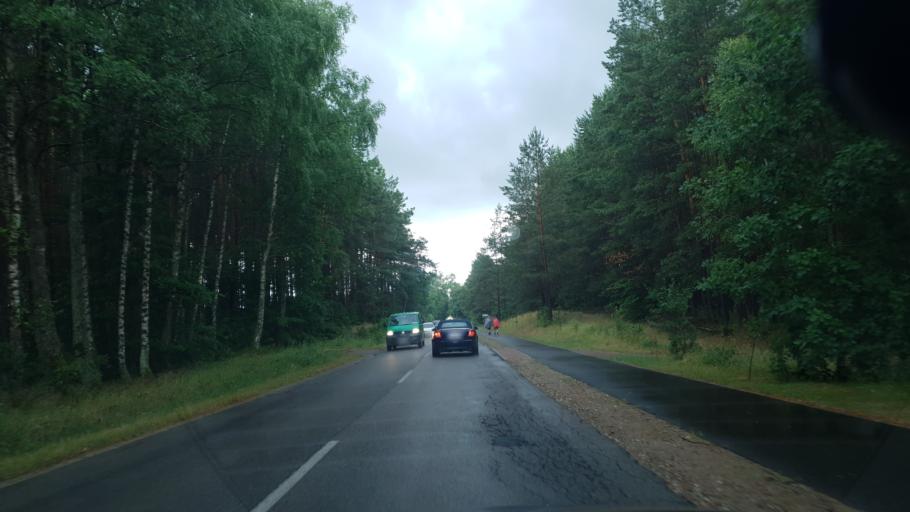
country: PL
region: Pomeranian Voivodeship
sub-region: Powiat kartuski
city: Stezyca
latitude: 54.2216
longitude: 17.9679
